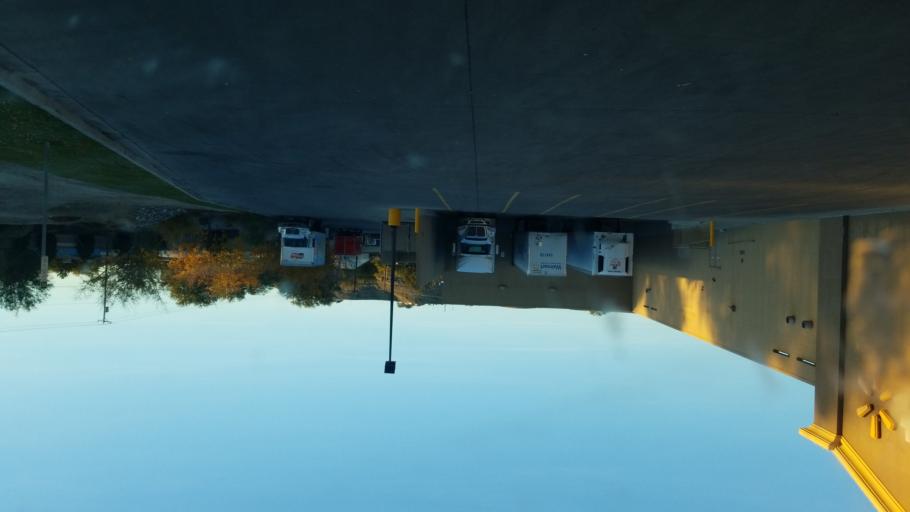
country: US
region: New Mexico
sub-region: San Juan County
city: Farmington
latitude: 36.7309
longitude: -108.2259
